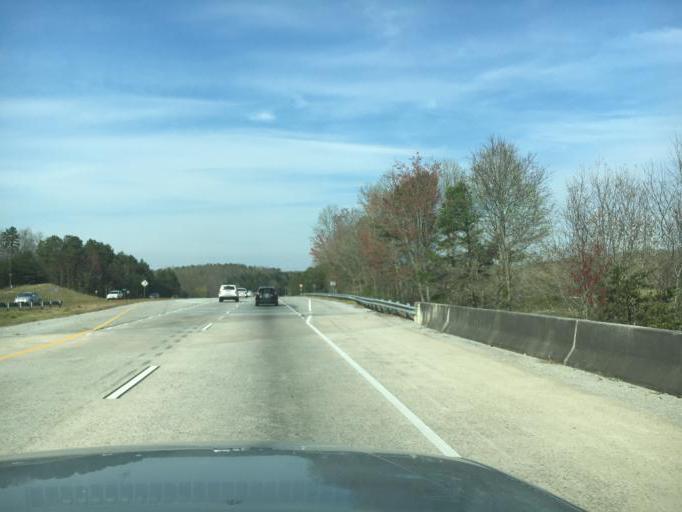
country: US
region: Georgia
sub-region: Hall County
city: Lula
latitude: 34.3822
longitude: -83.7105
